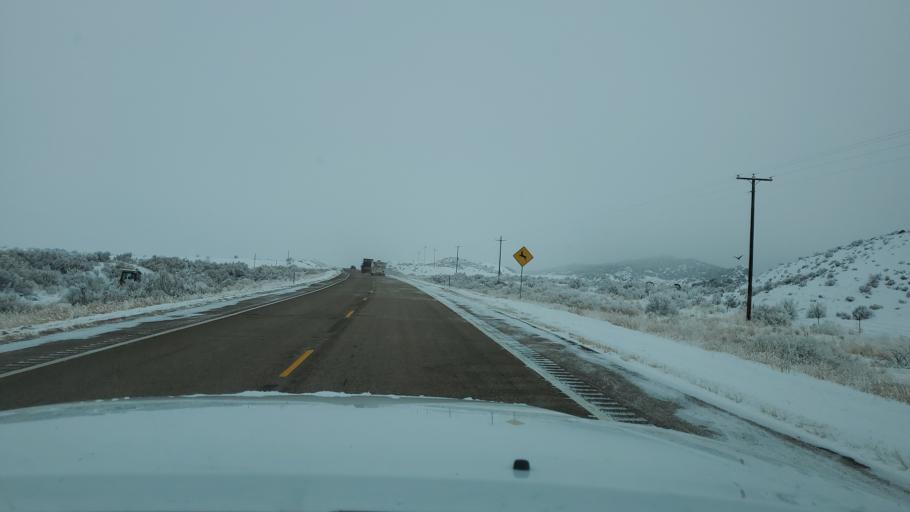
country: US
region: Colorado
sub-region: Rio Blanco County
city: Rangely
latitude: 40.2428
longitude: -108.9516
